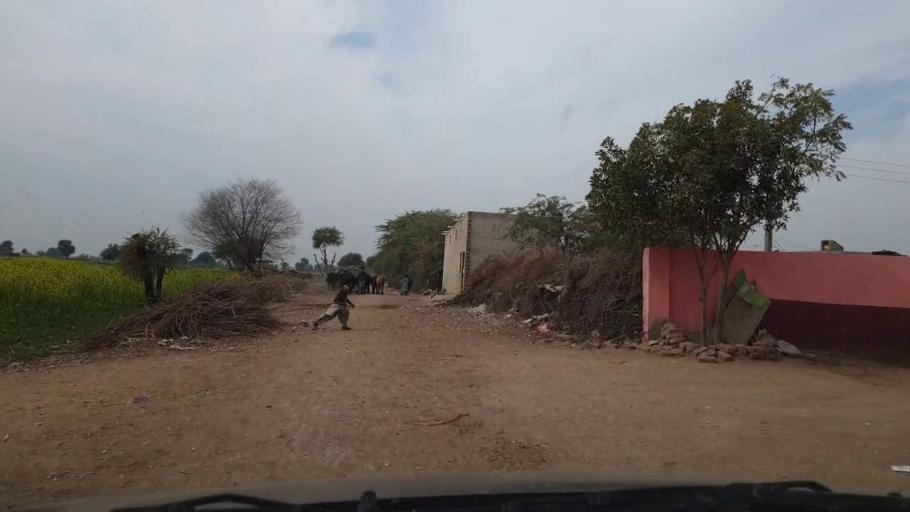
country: PK
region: Sindh
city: Sinjhoro
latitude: 26.0714
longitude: 68.8300
